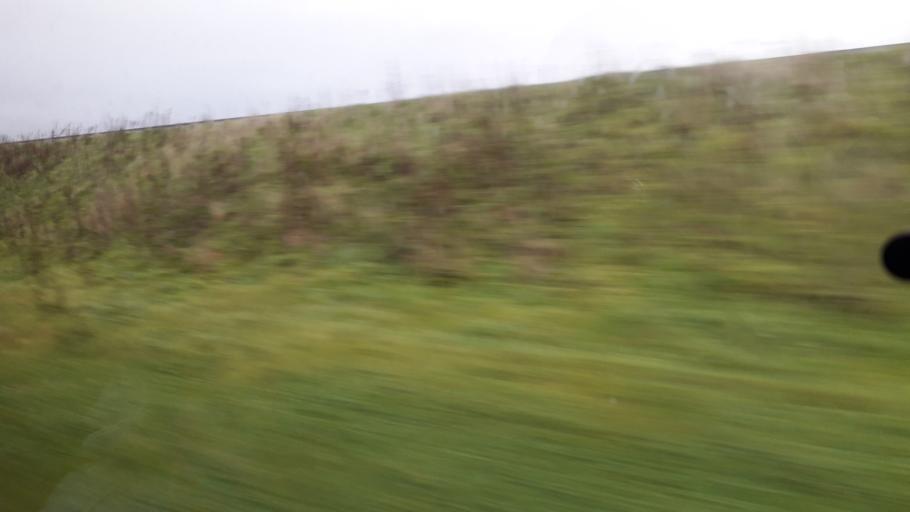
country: IE
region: Connaught
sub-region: County Galway
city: Athenry
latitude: 53.2925
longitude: -8.8084
